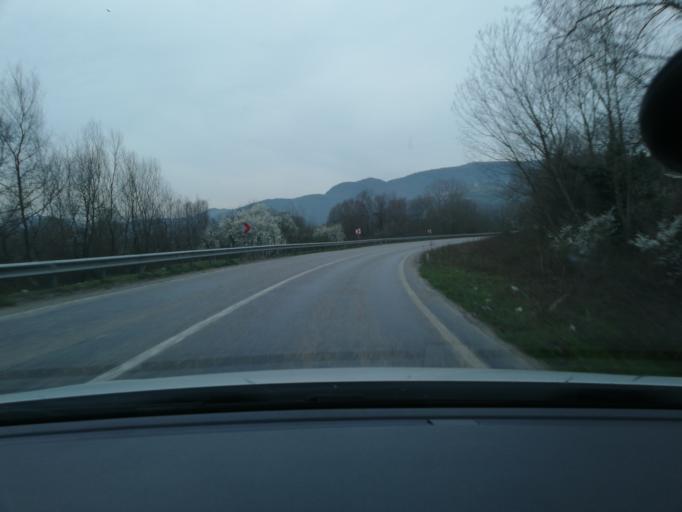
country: TR
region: Zonguldak
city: Saltukova
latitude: 41.5216
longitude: 32.0903
